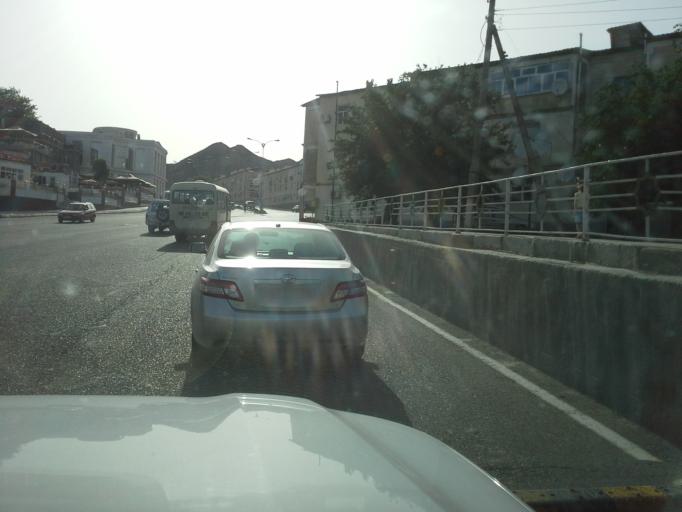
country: TM
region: Balkan
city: Turkmenbasy
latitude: 40.0023
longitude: 52.9839
